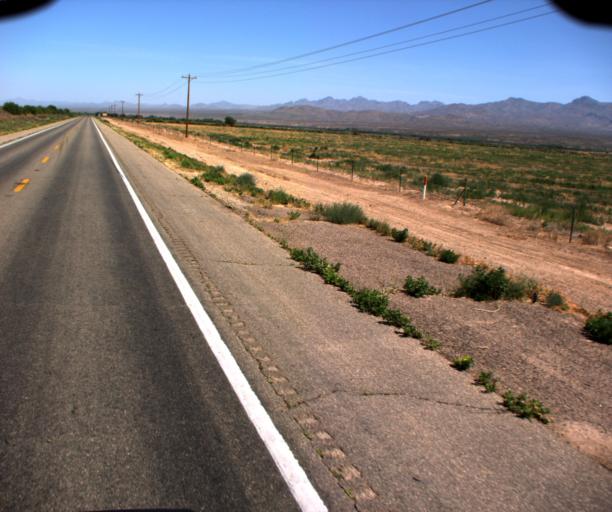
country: US
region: Arizona
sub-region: Graham County
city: Pima
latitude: 33.0015
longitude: -109.9437
